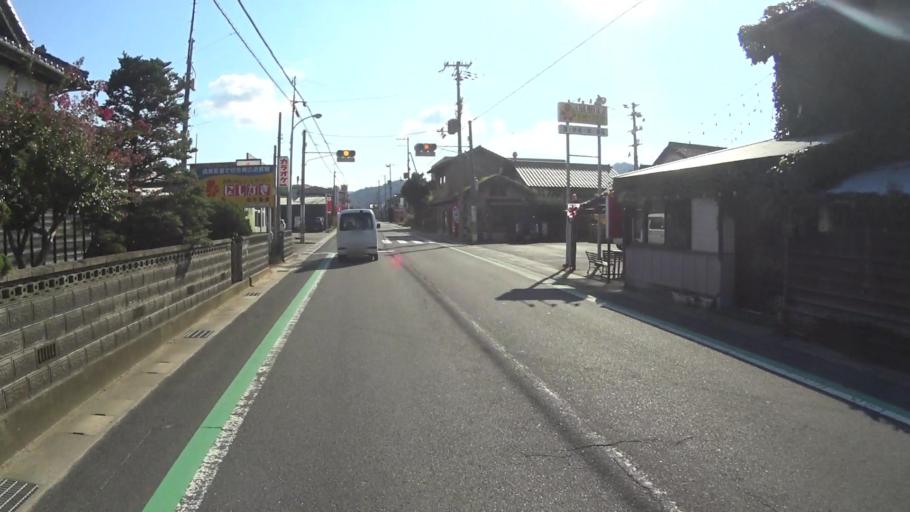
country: JP
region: Kyoto
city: Miyazu
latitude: 35.6862
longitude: 135.0327
